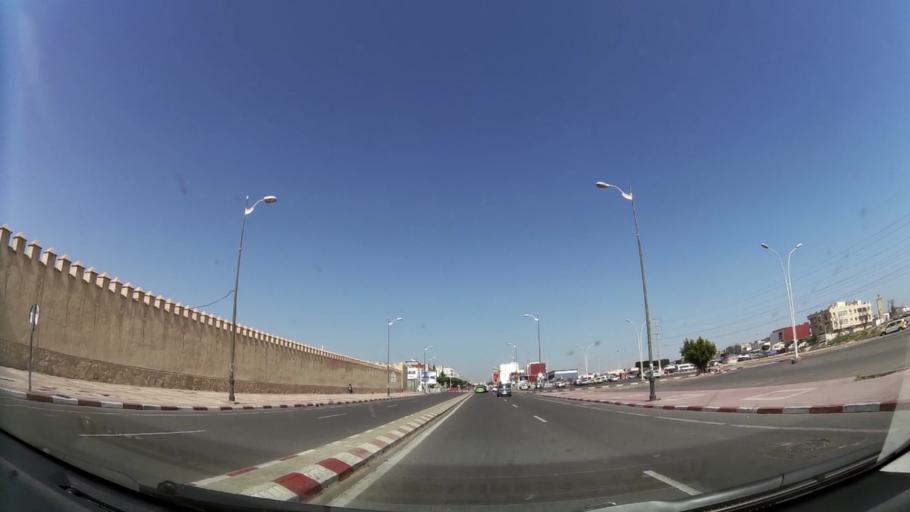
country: MA
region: Souss-Massa-Draa
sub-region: Agadir-Ida-ou-Tnan
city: Agadir
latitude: 30.4115
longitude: -9.5787
